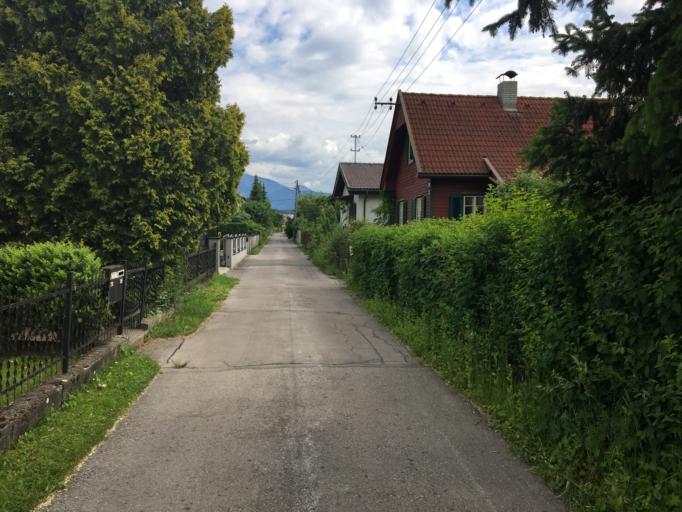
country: AT
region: Carinthia
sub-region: Klagenfurt am Woerthersee
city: Klagenfurt am Woerthersee
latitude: 46.5997
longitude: 14.2723
